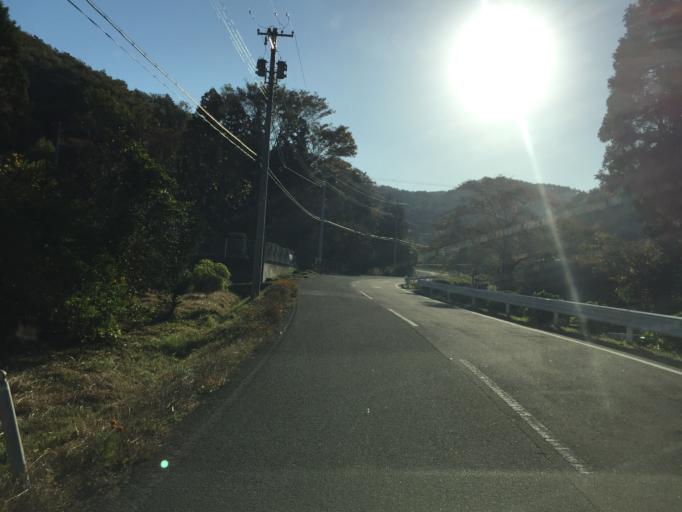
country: JP
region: Fukushima
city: Yanagawamachi-saiwaicho
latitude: 37.9219
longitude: 140.6140
